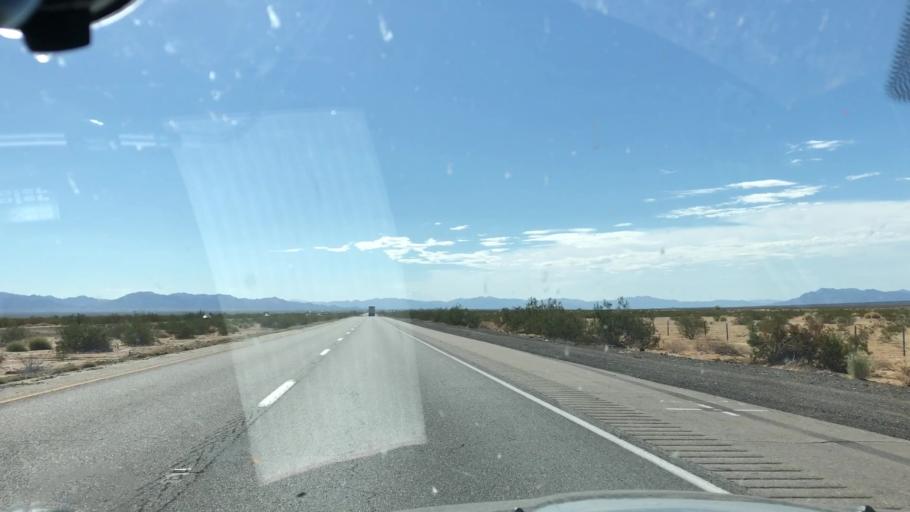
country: US
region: California
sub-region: Riverside County
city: Mesa Verde
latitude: 33.6261
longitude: -115.0554
